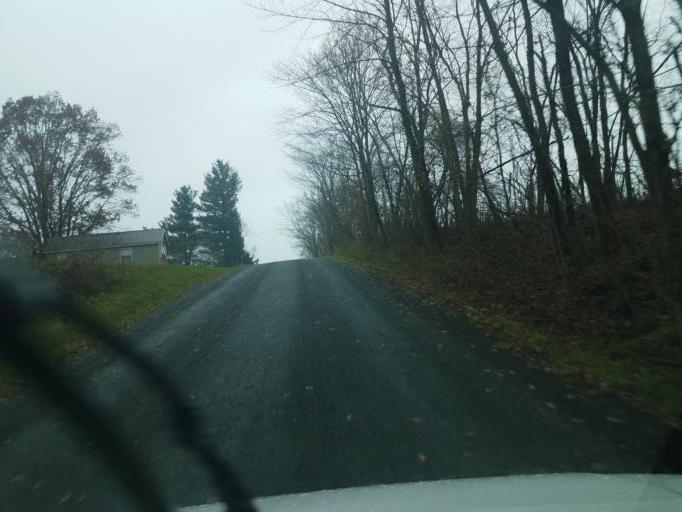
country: US
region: Ohio
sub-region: Morrow County
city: Mount Gilead
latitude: 40.5606
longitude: -82.7006
